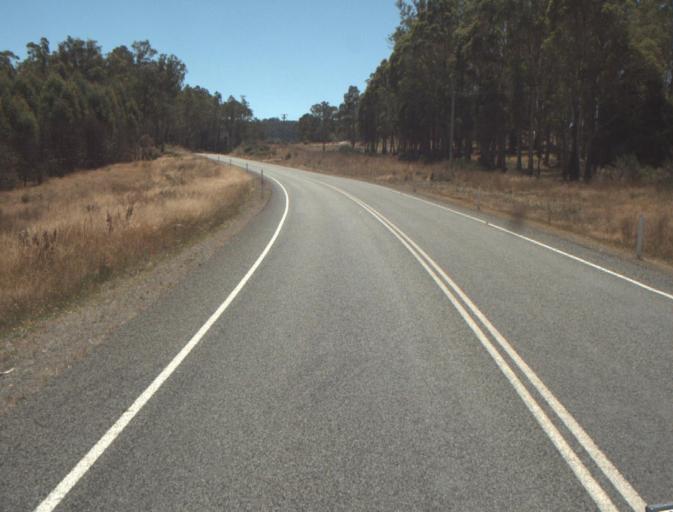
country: AU
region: Tasmania
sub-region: Launceston
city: Newstead
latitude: -41.3395
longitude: 147.3471
